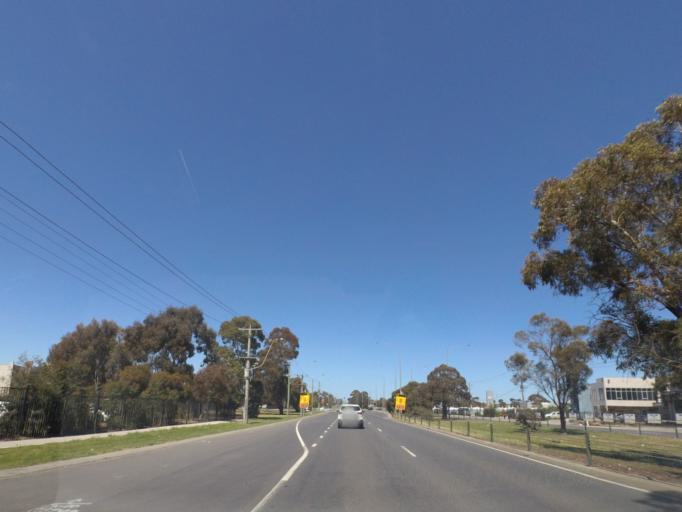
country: AU
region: Victoria
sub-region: Hume
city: Craigieburn
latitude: -37.6148
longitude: 144.9470
